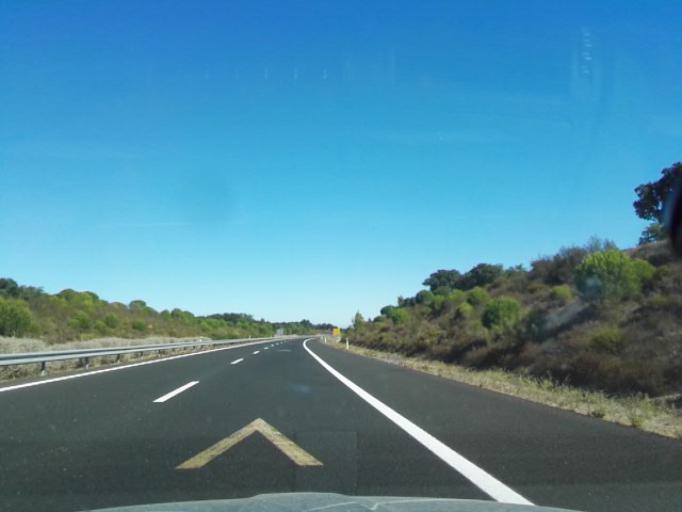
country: PT
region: Santarem
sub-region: Benavente
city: Poceirao
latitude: 38.8797
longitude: -8.7939
